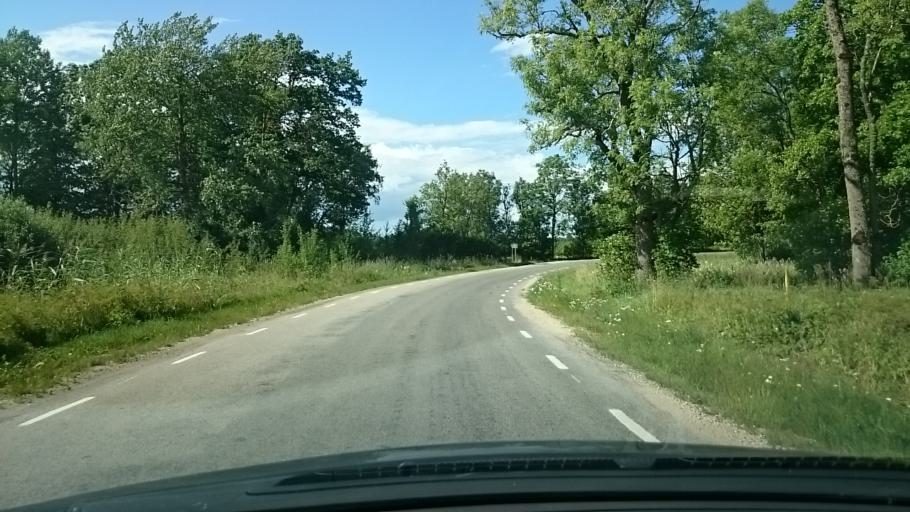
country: EE
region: Laeaene
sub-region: Haapsalu linn
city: Haapsalu
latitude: 59.0362
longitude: 23.5100
